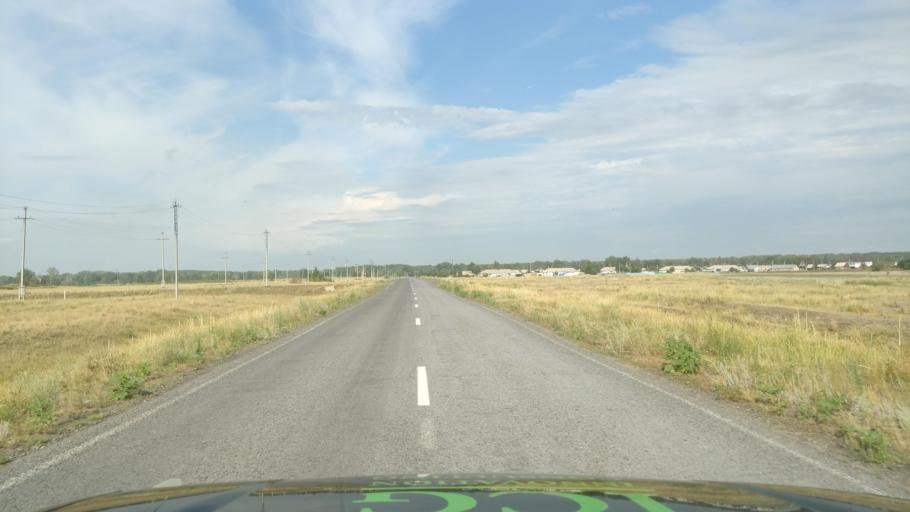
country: KZ
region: Pavlodar
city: Leninskiy
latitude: 52.4777
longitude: 76.8278
